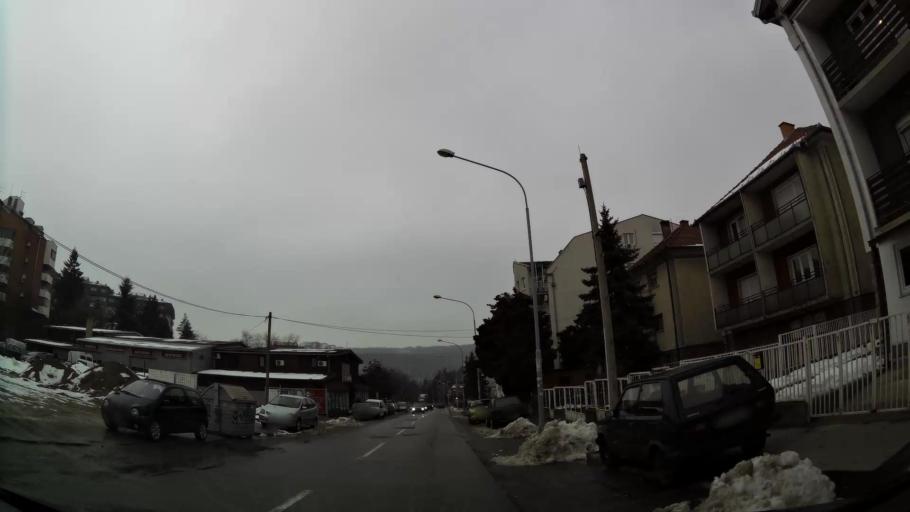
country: RS
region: Central Serbia
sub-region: Belgrade
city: Rakovica
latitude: 44.7498
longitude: 20.4542
